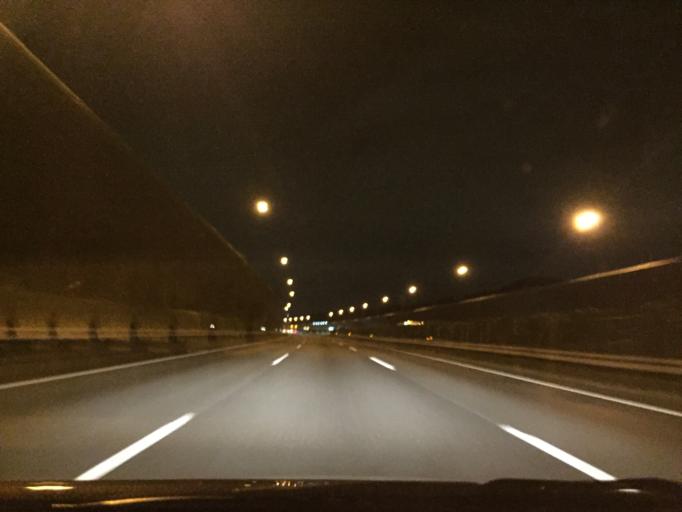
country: JP
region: Kanagawa
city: Isehara
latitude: 35.4025
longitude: 139.2902
